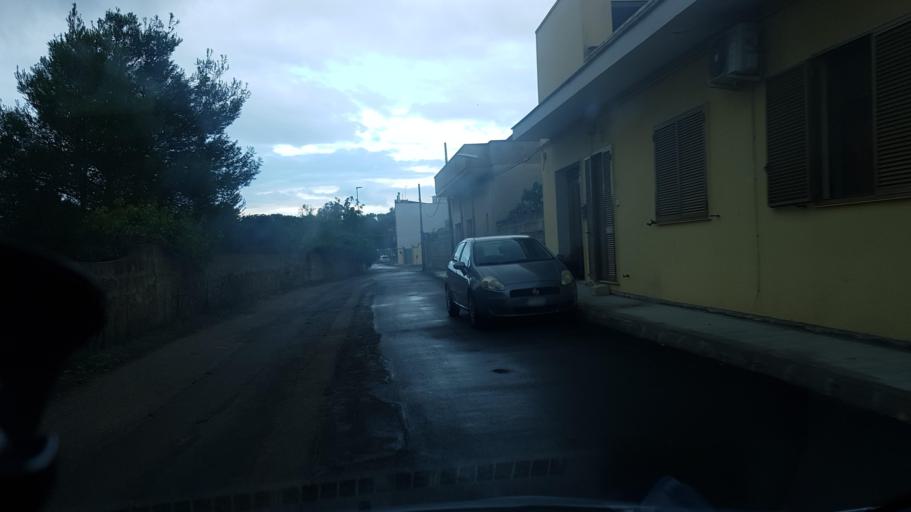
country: IT
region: Apulia
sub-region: Provincia di Lecce
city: Novoli
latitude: 40.3659
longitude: 18.0715
